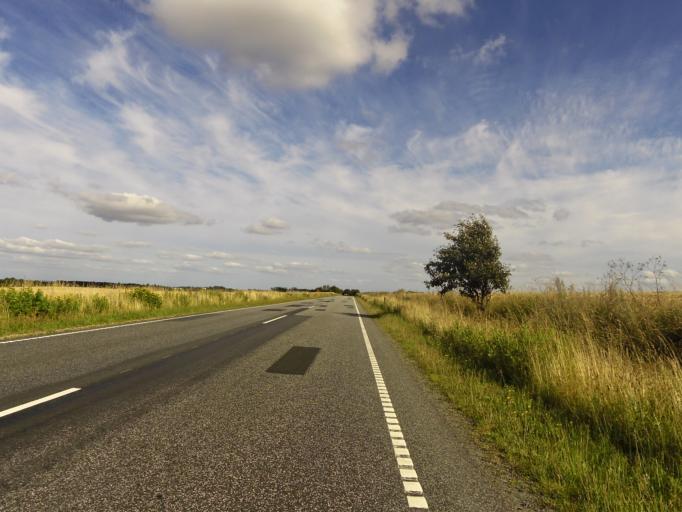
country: DK
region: South Denmark
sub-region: Tonder Kommune
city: Toftlund
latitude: 55.2215
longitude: 9.0107
